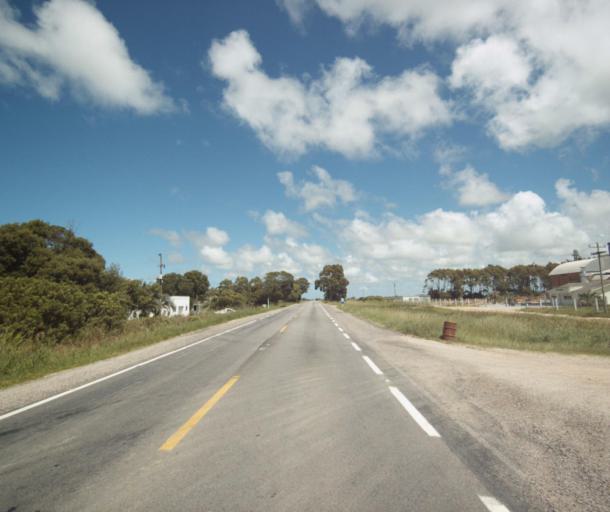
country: UY
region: Cerro Largo
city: Rio Branco
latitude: -32.8869
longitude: -52.7221
